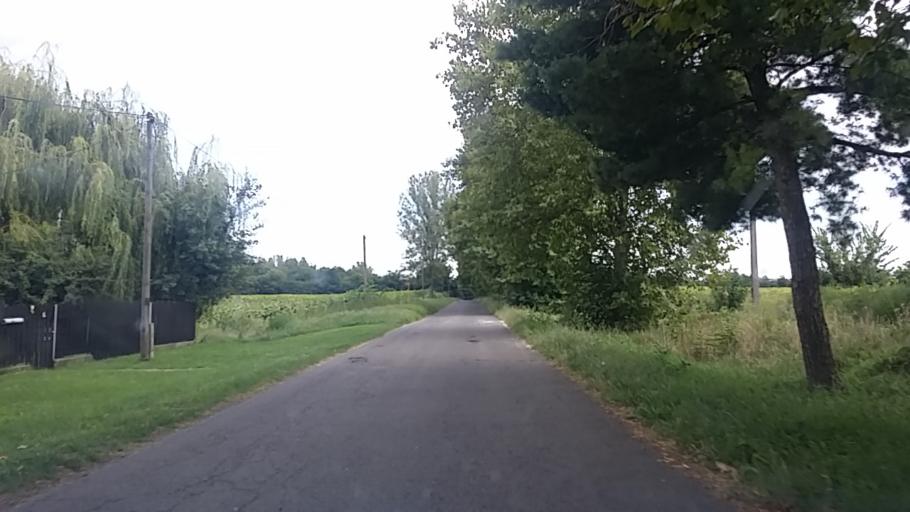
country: HU
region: Tolna
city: Szedres
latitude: 46.5285
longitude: 18.6375
